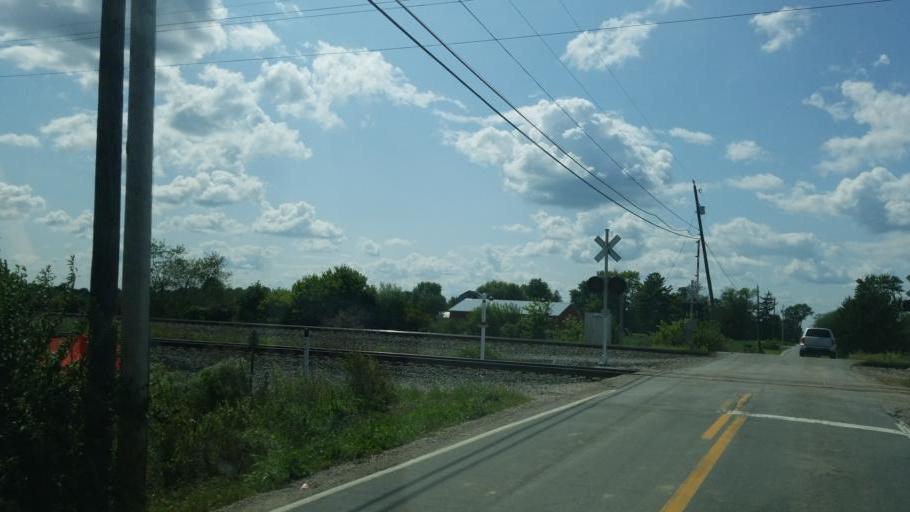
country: US
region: Ohio
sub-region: Delaware County
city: Lewis Center
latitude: 40.2265
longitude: -83.0113
